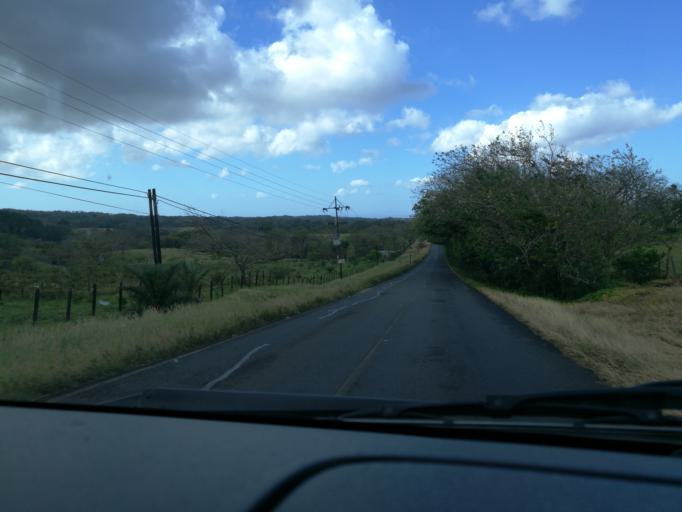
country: CR
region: Alajuela
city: Bijagua
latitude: 10.6642
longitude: -85.0909
